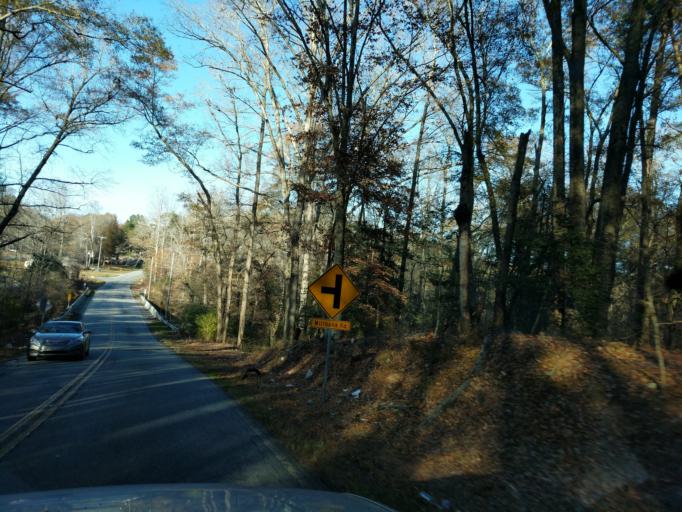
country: US
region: South Carolina
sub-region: Spartanburg County
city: Wellford
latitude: 34.9105
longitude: -82.0849
